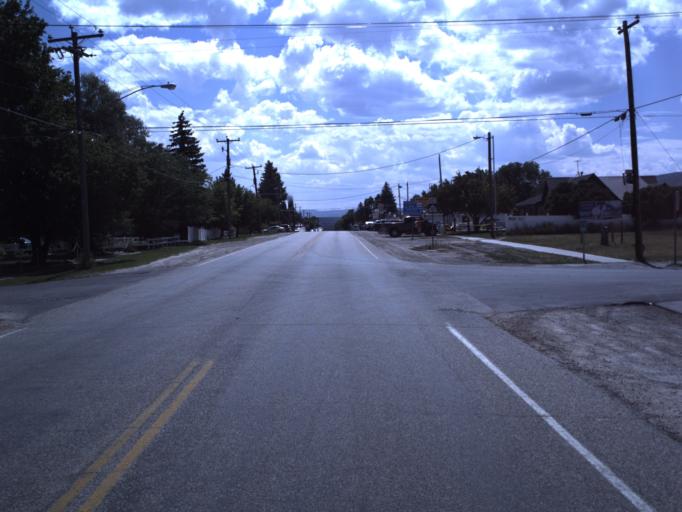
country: US
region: Idaho
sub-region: Bear Lake County
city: Paris
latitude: 41.9500
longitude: -111.3933
